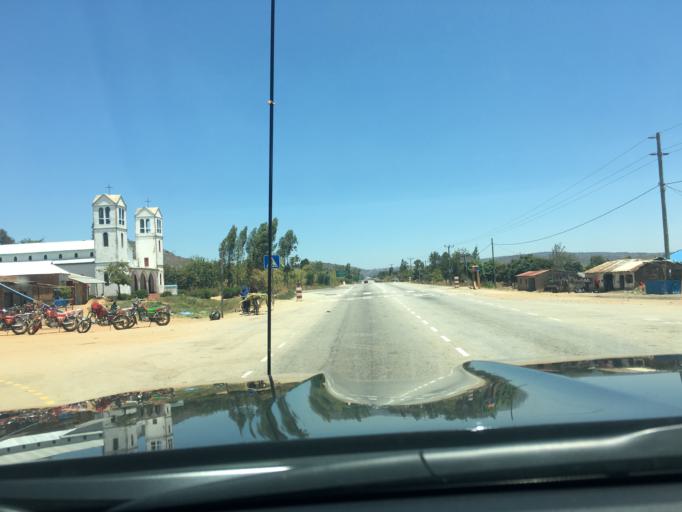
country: TZ
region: Iringa
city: Iringa
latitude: -7.9044
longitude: 35.5899
